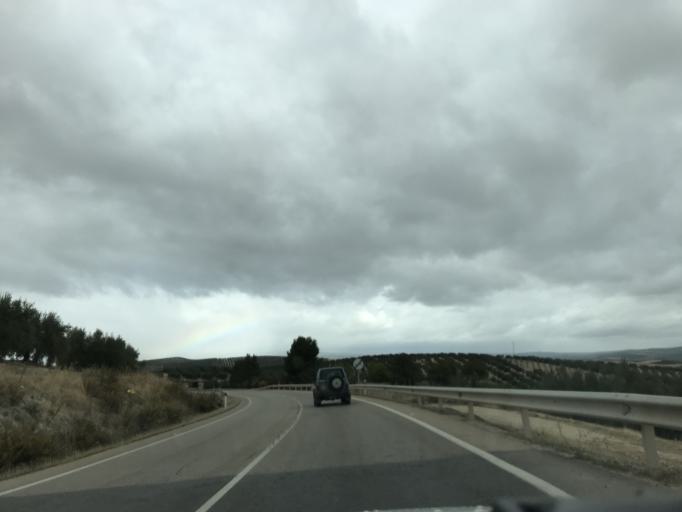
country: ES
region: Andalusia
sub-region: Provincia de Jaen
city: Peal de Becerro
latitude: 37.9207
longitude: -3.1322
